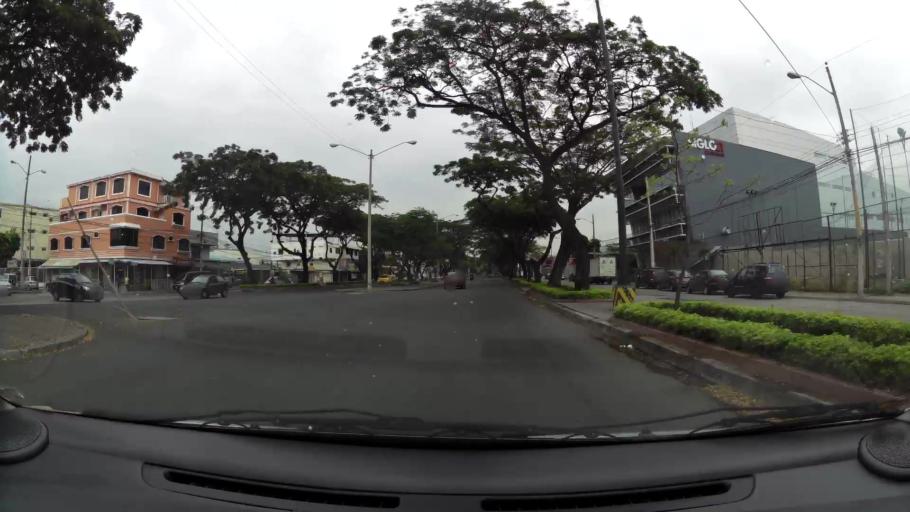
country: EC
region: Guayas
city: Eloy Alfaro
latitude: -2.1443
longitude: -79.8869
